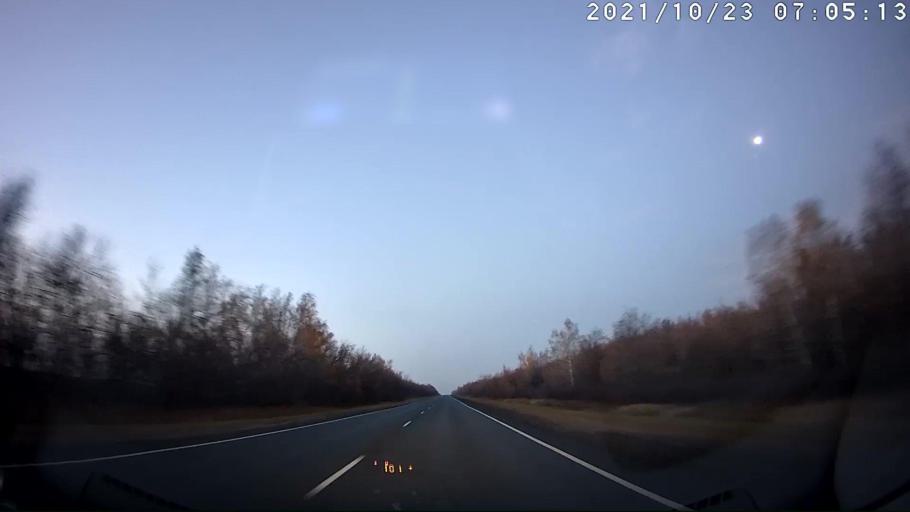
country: RU
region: Saratov
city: Khvalynsk
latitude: 52.6078
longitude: 48.1544
